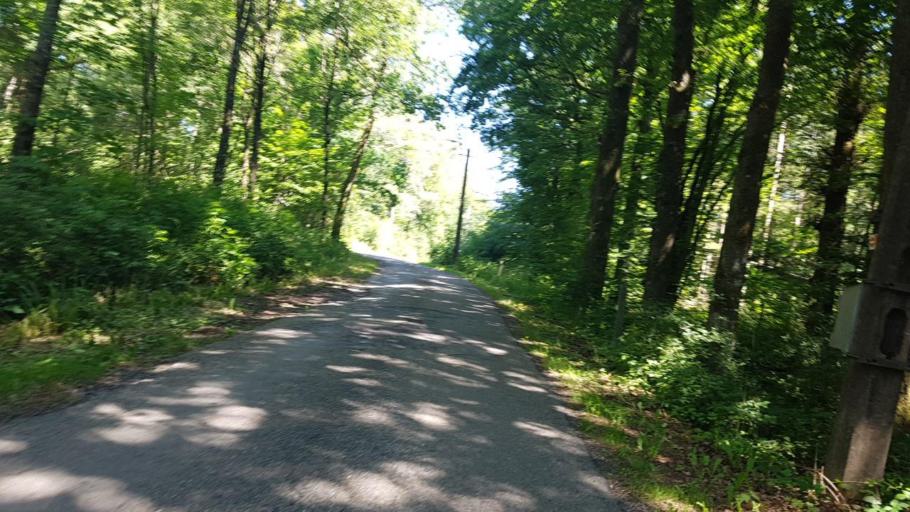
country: BE
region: Wallonia
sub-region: Province du Hainaut
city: Momignies
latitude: 50.1050
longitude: 4.2308
